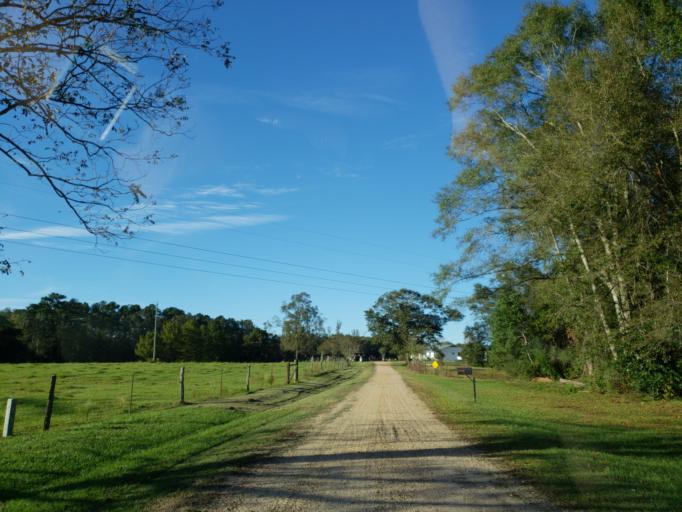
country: US
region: Mississippi
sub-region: Perry County
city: Richton
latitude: 31.3662
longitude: -88.8113
